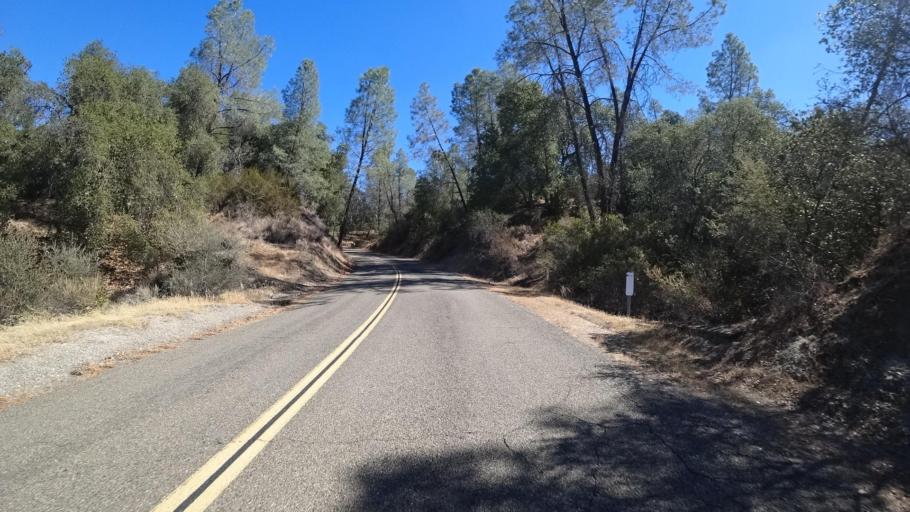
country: US
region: California
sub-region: San Luis Obispo County
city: San Miguel
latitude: 35.9094
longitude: -120.5464
